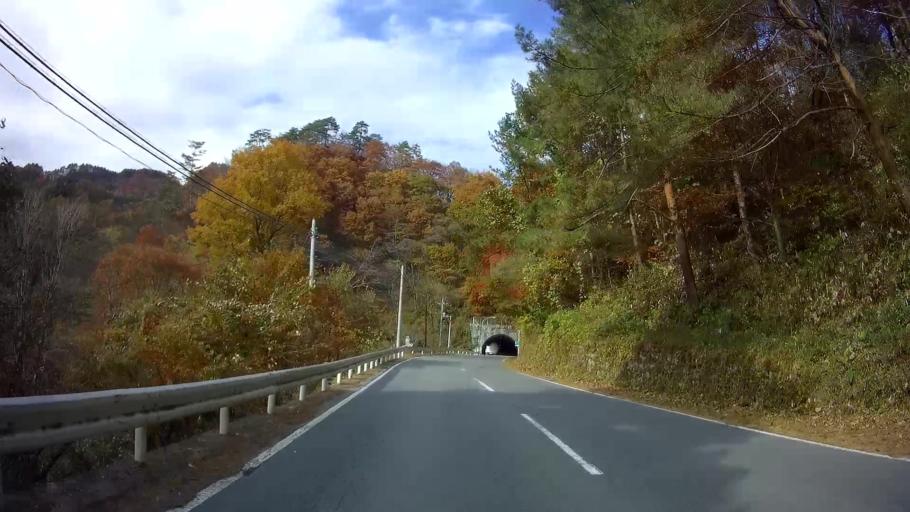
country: JP
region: Gunma
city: Nakanojomachi
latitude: 36.6476
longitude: 138.6506
